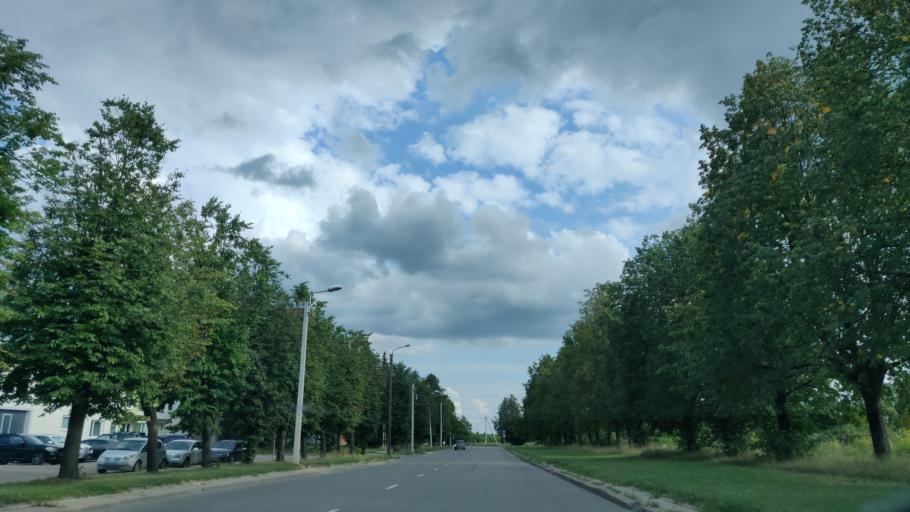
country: LT
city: Baltoji Voke
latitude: 54.6218
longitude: 25.1428
